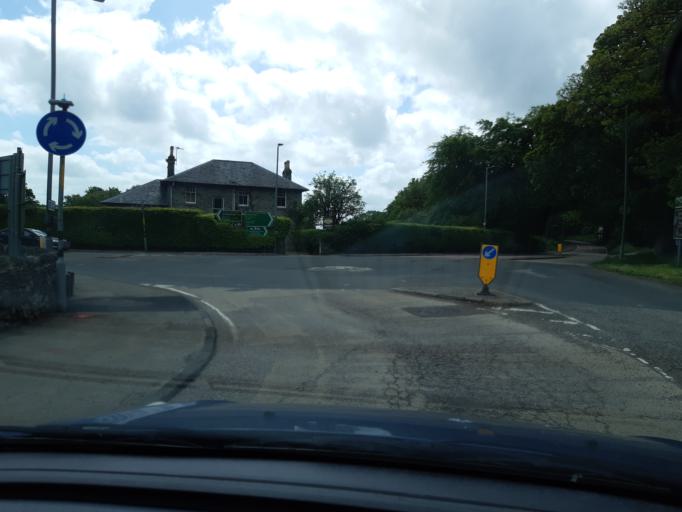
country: GB
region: Scotland
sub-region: Argyll and Bute
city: Lochgilphead
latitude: 56.0377
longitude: -5.4416
